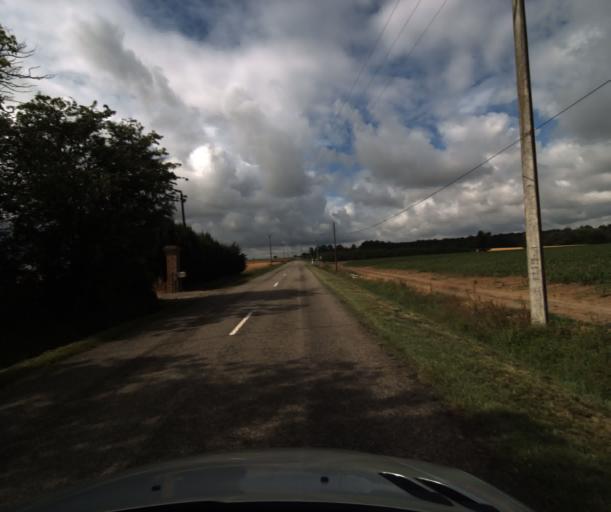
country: FR
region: Midi-Pyrenees
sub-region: Departement du Tarn-et-Garonne
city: Lavit
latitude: 43.9906
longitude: 0.9796
